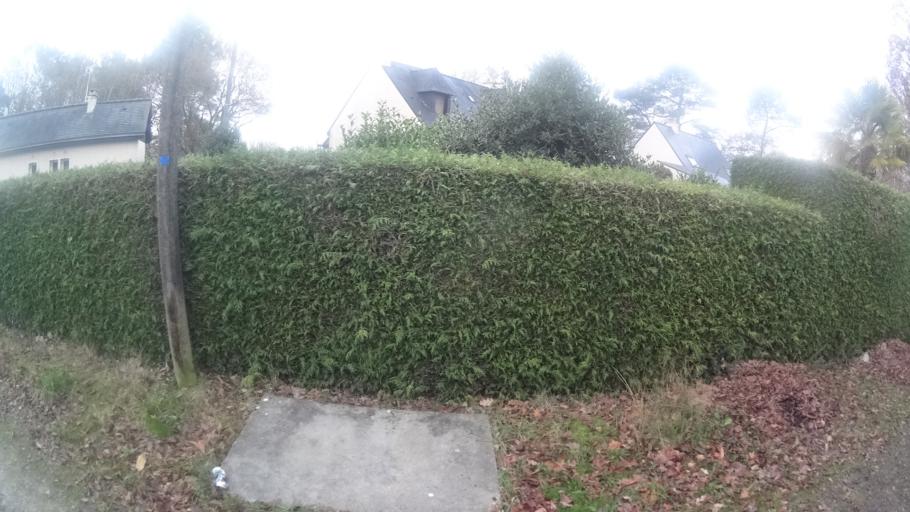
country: FR
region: Pays de la Loire
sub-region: Departement de la Loire-Atlantique
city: Saint-Nicolas-de-Redon
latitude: 47.6413
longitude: -2.0424
